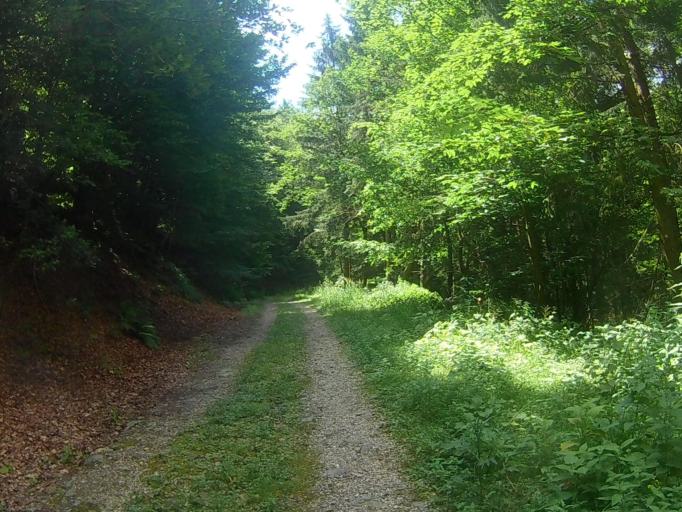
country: SI
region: Selnica ob Dravi
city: Selnica ob Dravi
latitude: 46.5198
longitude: 15.4890
